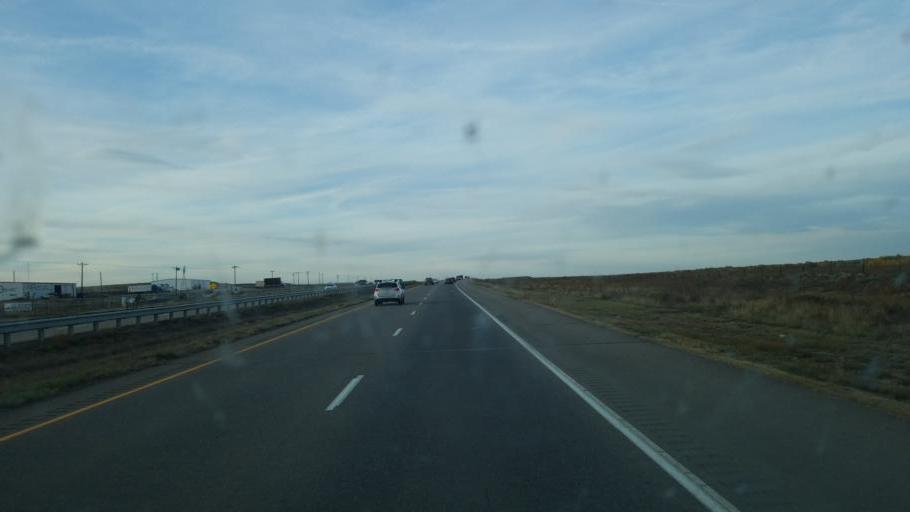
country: US
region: Colorado
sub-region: Pueblo County
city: Pueblo West
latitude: 38.3626
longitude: -104.6208
